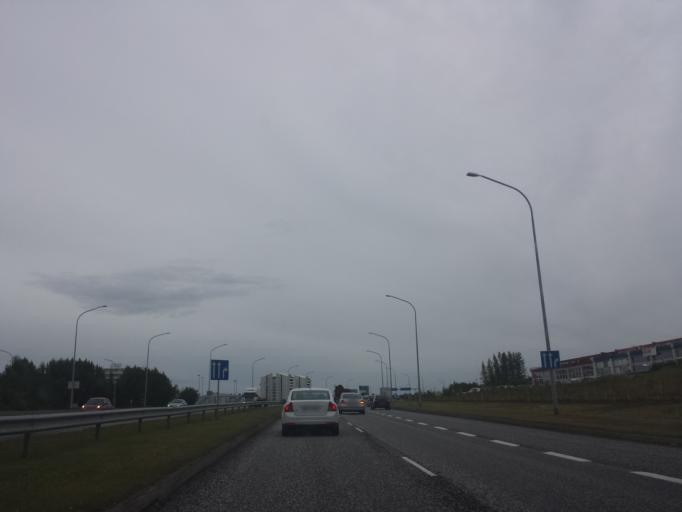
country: IS
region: Capital Region
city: Reykjavik
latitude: 64.1113
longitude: -21.8444
